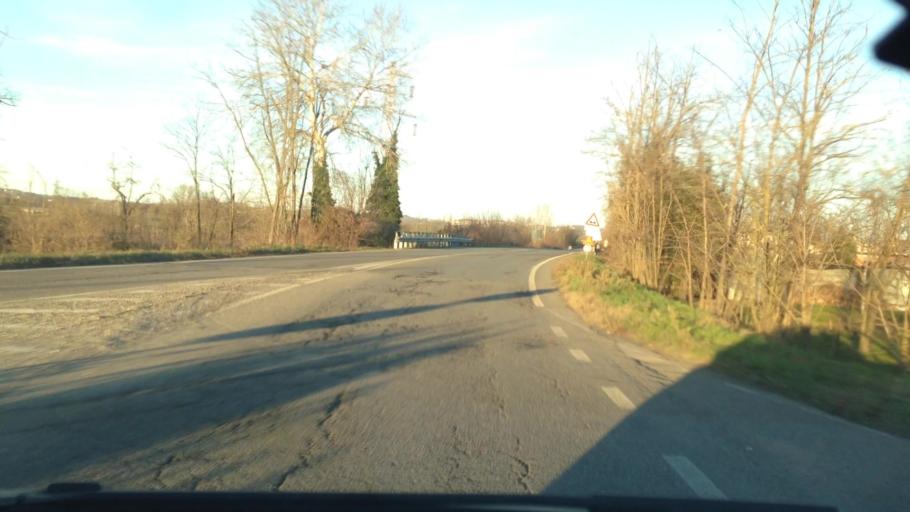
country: IT
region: Piedmont
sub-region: Provincia di Alessandria
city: Solero
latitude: 44.9183
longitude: 8.4978
